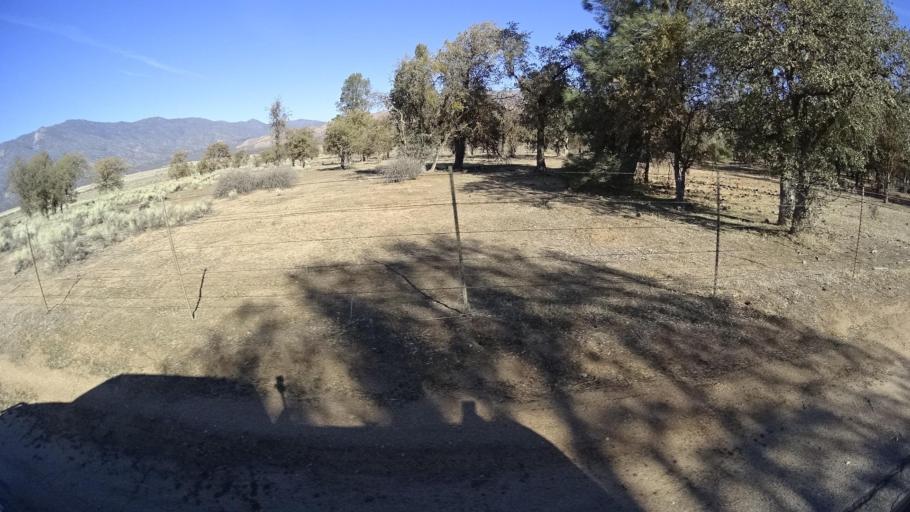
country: US
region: California
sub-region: Kern County
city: Bodfish
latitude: 35.4020
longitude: -118.5118
